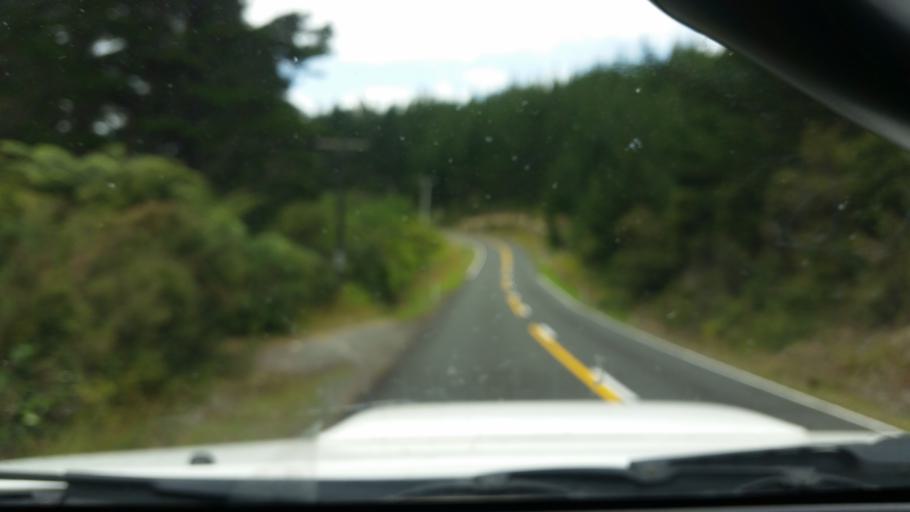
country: NZ
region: Northland
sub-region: Kaipara District
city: Dargaville
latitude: -35.8159
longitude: 173.7225
